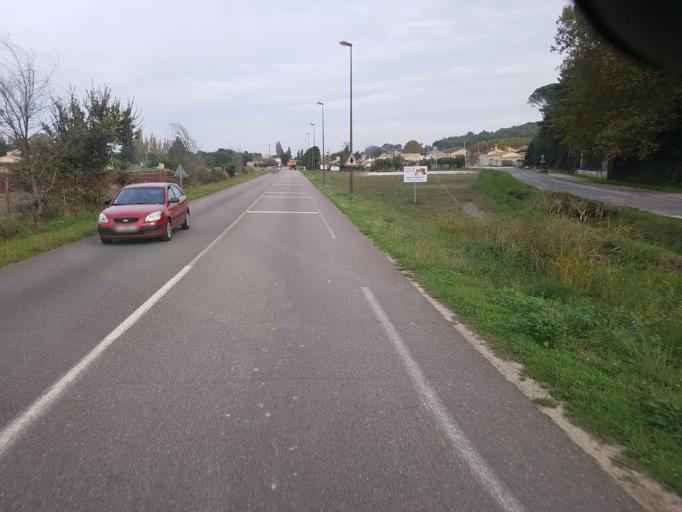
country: FR
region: Provence-Alpes-Cote d'Azur
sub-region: Departement des Bouches-du-Rhone
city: Barbentane
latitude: 43.9025
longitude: 4.7467
